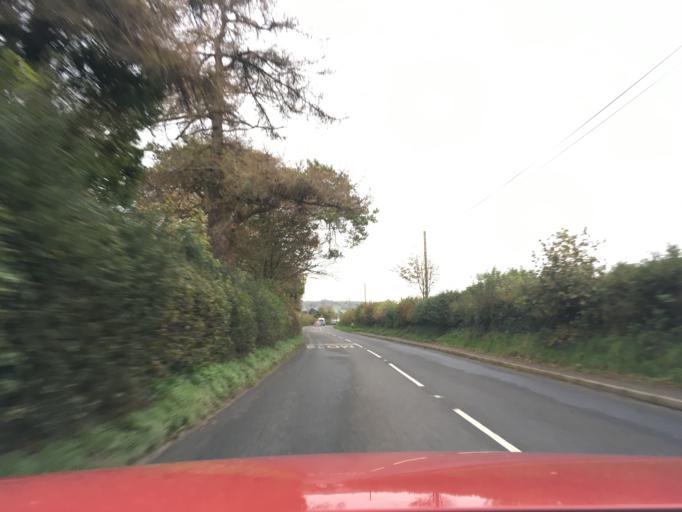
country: GB
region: England
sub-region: Dorset
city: Sherborne
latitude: 50.9559
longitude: -2.5347
